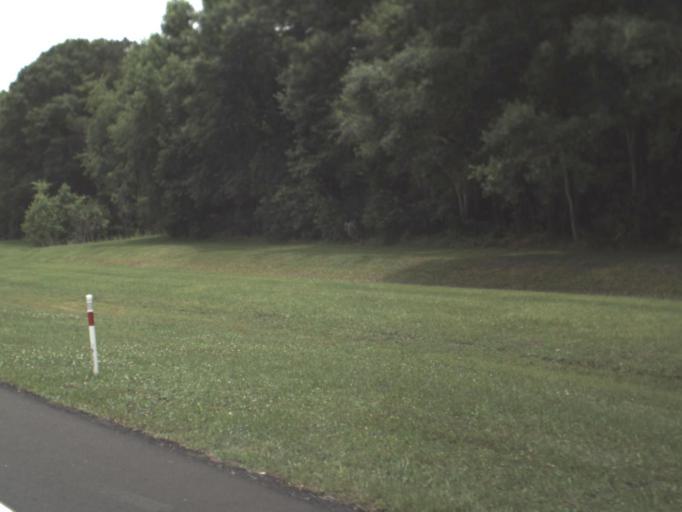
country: US
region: Florida
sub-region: Nassau County
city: Nassau Village-Ratliff
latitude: 30.4887
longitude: -81.6759
